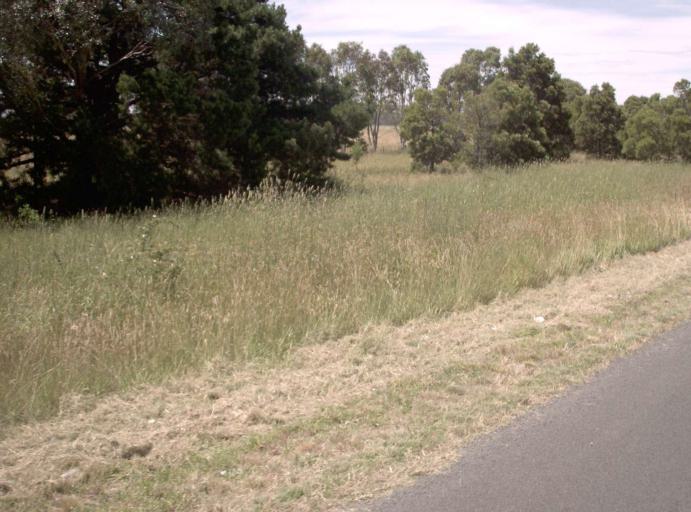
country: AU
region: Victoria
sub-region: Wellington
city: Heyfield
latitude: -38.1587
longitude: 146.7368
